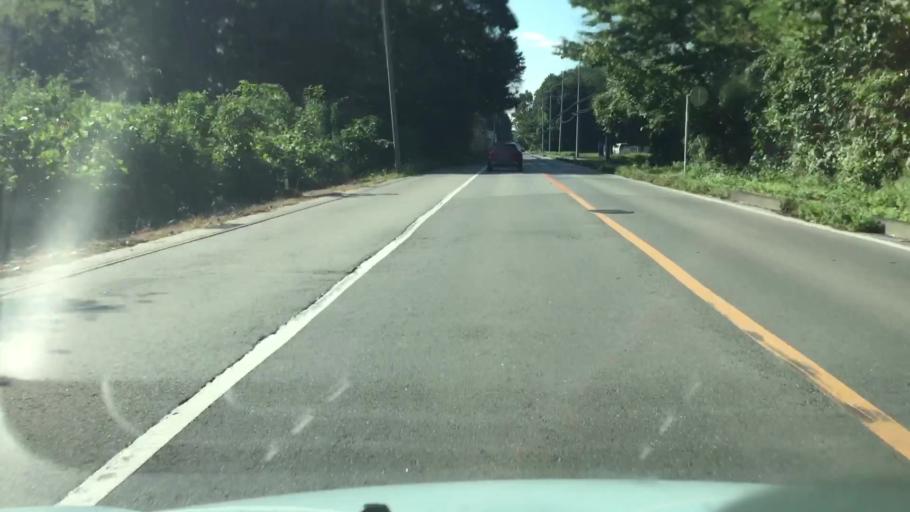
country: JP
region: Tochigi
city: Utsunomiya-shi
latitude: 36.5742
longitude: 139.9791
